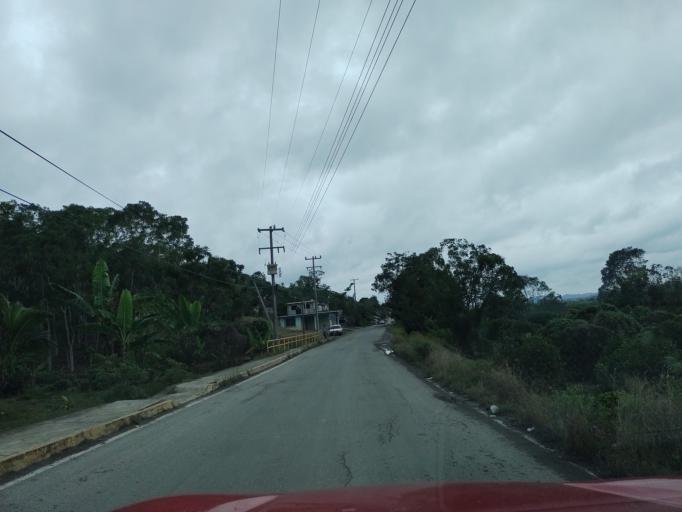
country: MX
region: Puebla
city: Espinal
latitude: 20.2622
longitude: -97.3708
